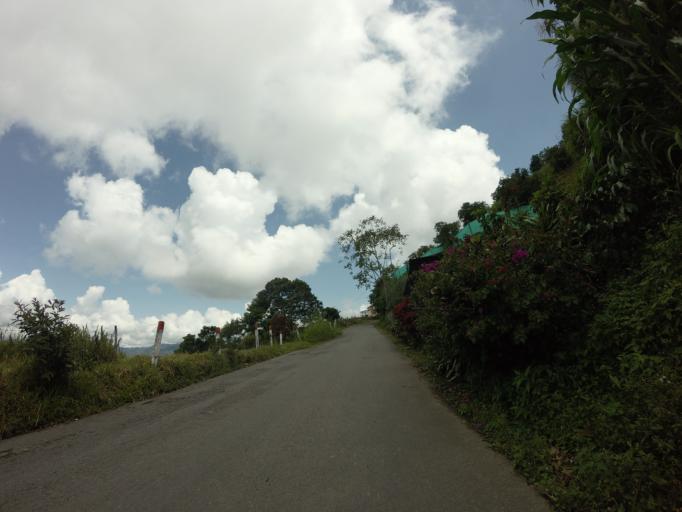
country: CO
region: Caldas
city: Marquetalia
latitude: 5.2997
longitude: -75.0617
